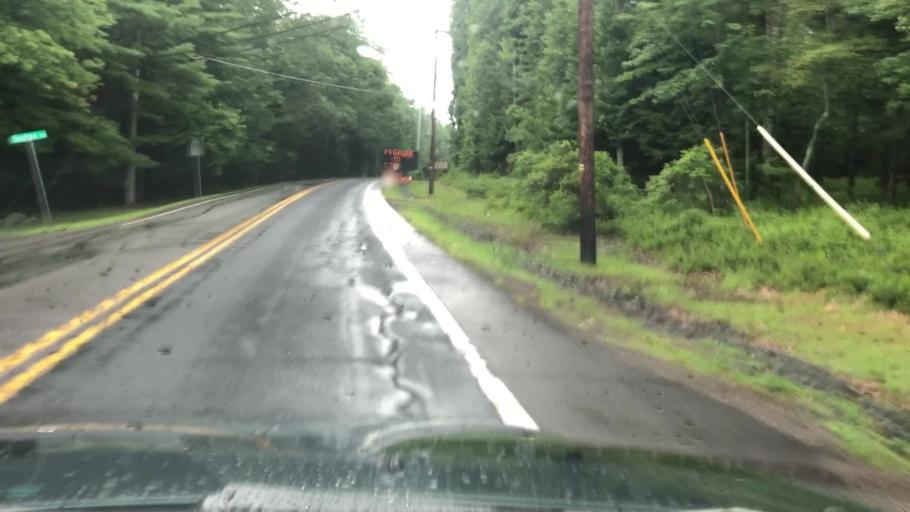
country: US
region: Pennsylvania
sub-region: Monroe County
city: Mountainhome
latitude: 41.2277
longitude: -75.2328
